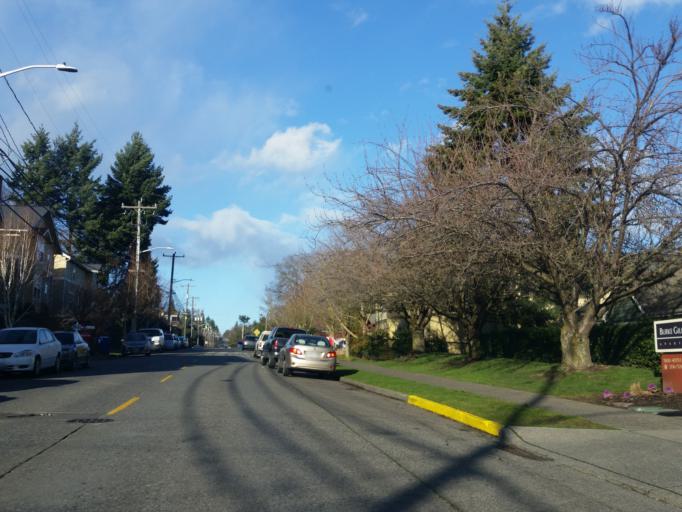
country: US
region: Washington
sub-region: King County
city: Yarrow Point
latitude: 47.6662
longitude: -122.2848
